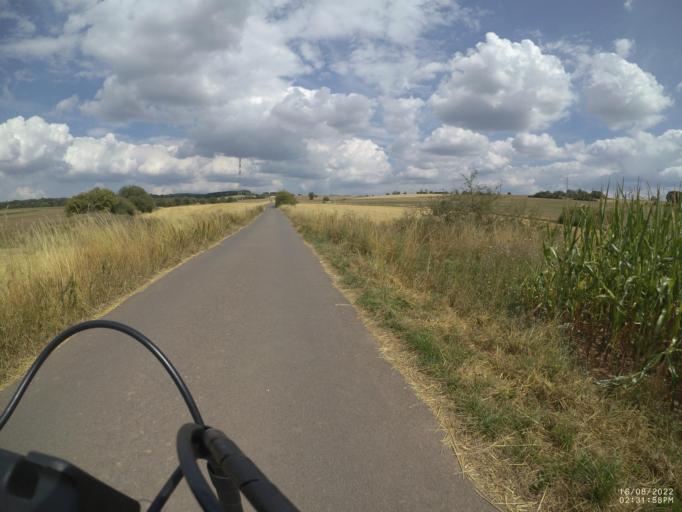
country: DE
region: Rheinland-Pfalz
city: Hillesheim
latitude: 50.3059
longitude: 6.6784
